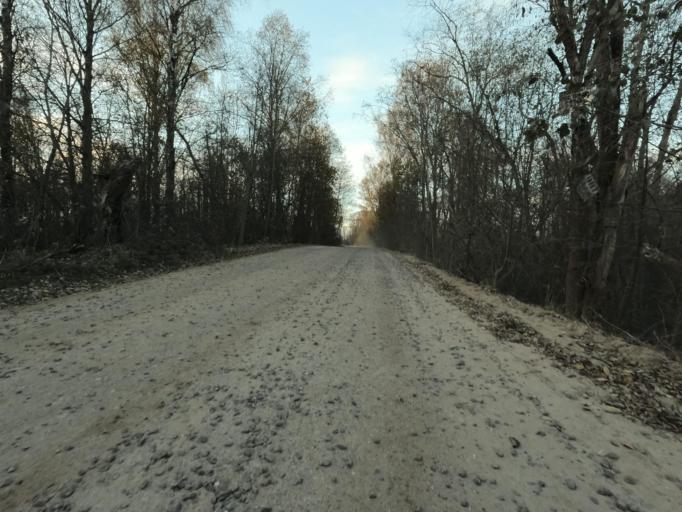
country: RU
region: Leningrad
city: Mga
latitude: 59.7734
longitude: 31.2260
